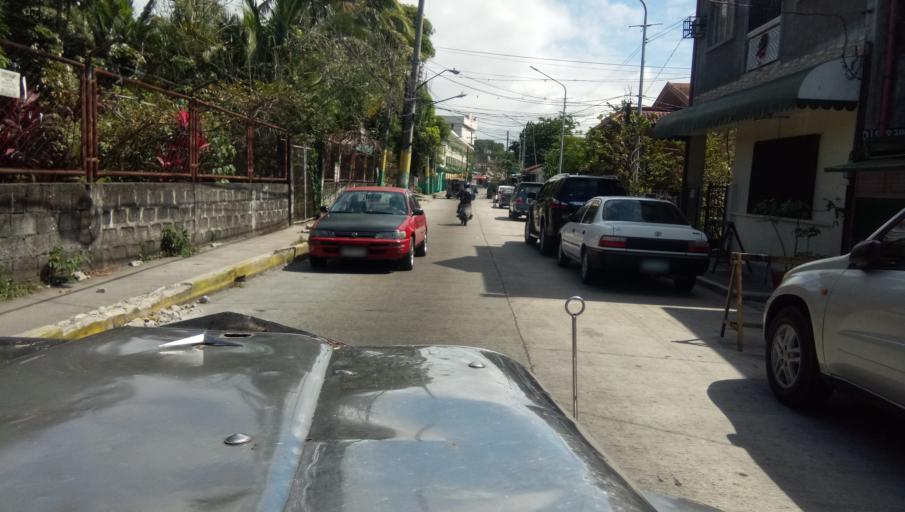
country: PH
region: Calabarzon
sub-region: Province of Cavite
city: Dasmarinas
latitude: 14.3274
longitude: 120.9343
